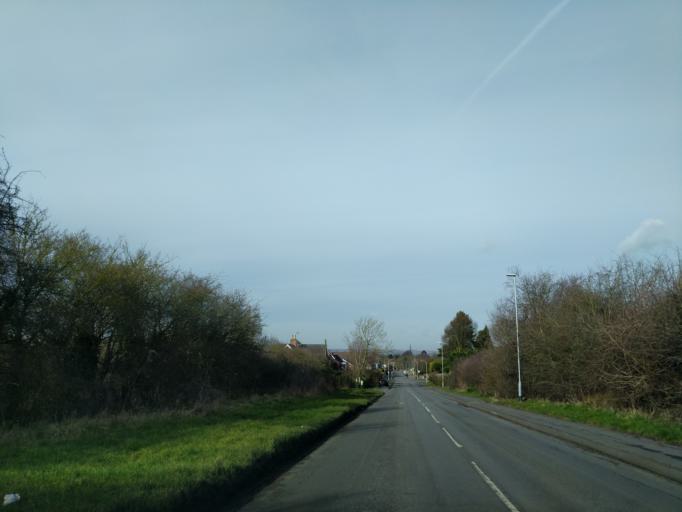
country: GB
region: England
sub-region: Nottinghamshire
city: Cotgrave
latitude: 52.9044
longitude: -1.0383
